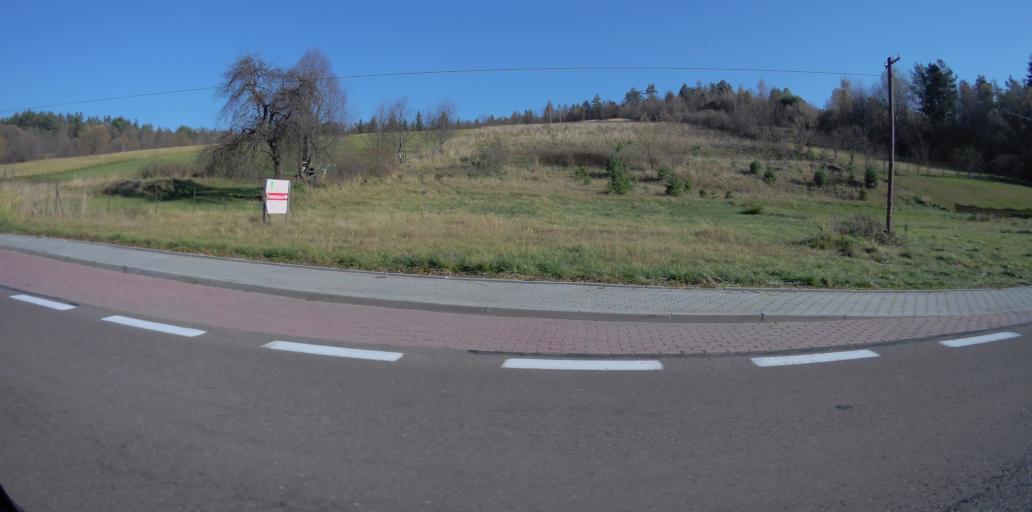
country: PL
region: Subcarpathian Voivodeship
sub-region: Powiat bieszczadzki
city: Ustrzyki Dolne
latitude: 49.5386
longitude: 22.5942
